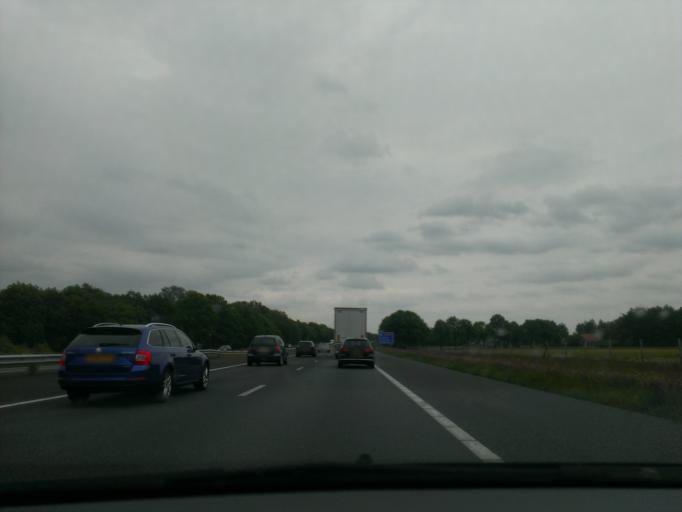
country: NL
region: Overijssel
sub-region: Gemeente Almelo
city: Almelo
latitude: 52.3169
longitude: 6.6791
